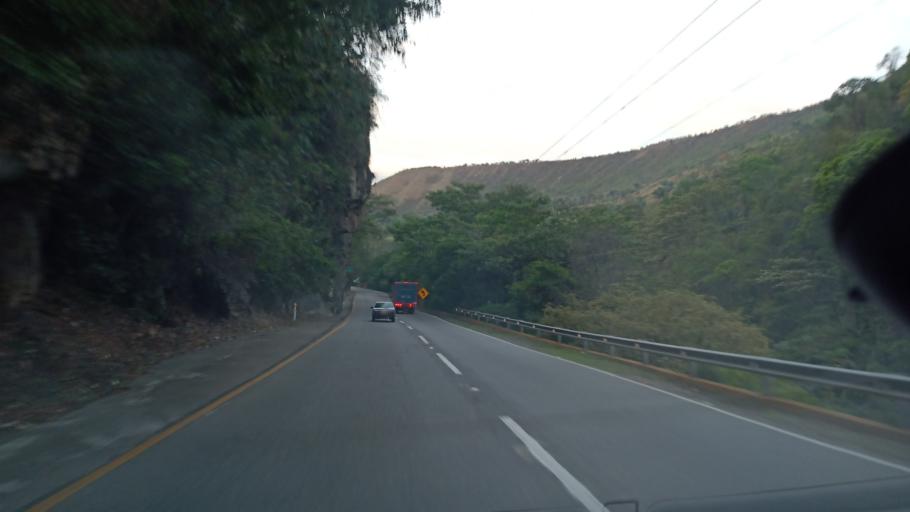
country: CO
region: Cundinamarca
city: Nilo
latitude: 4.2668
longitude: -74.5836
